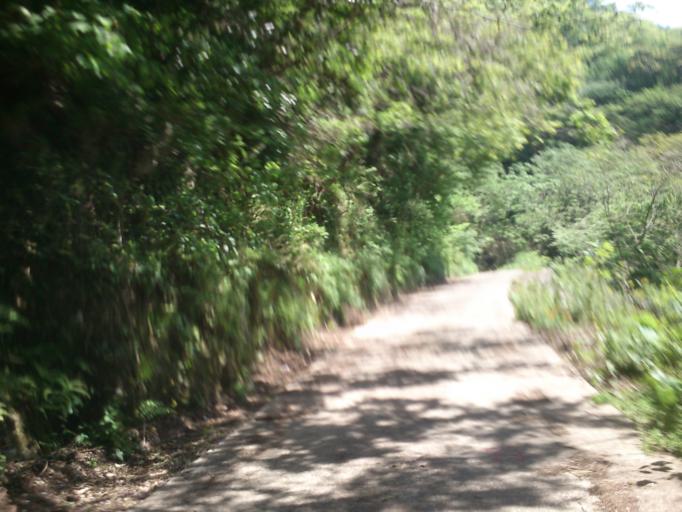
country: JP
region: Kyoto
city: Miyazu
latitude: 35.7160
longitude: 135.1363
